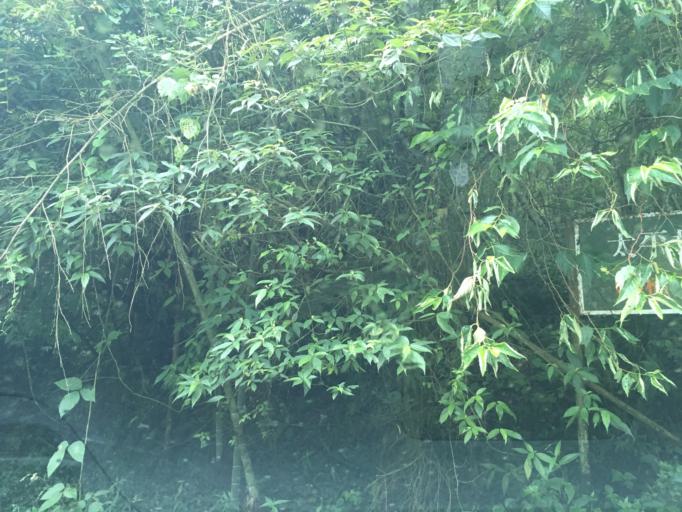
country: TW
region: Taiwan
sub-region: Yunlin
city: Douliu
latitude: 23.5601
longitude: 120.6101
